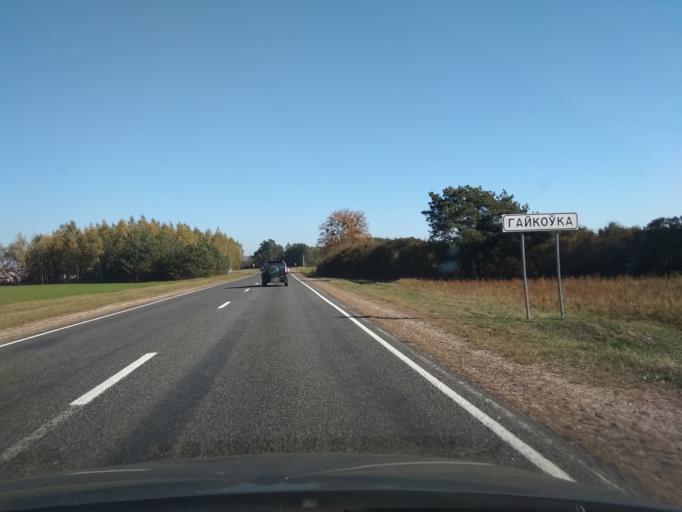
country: BY
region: Brest
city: Kobryn
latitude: 52.1156
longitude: 24.3009
